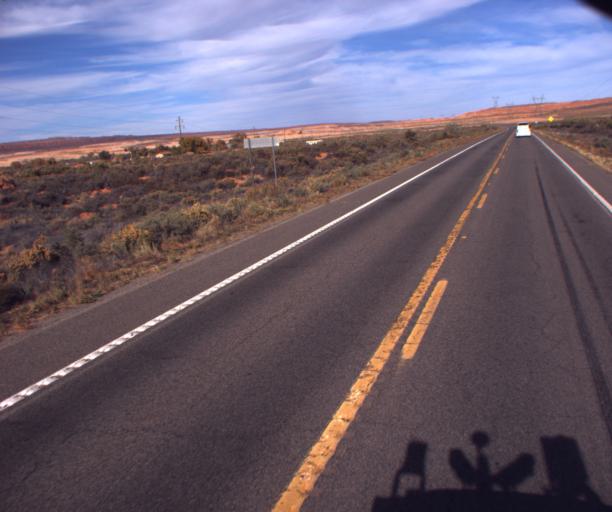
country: US
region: Arizona
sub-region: Navajo County
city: Kayenta
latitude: 36.8443
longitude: -109.8390
